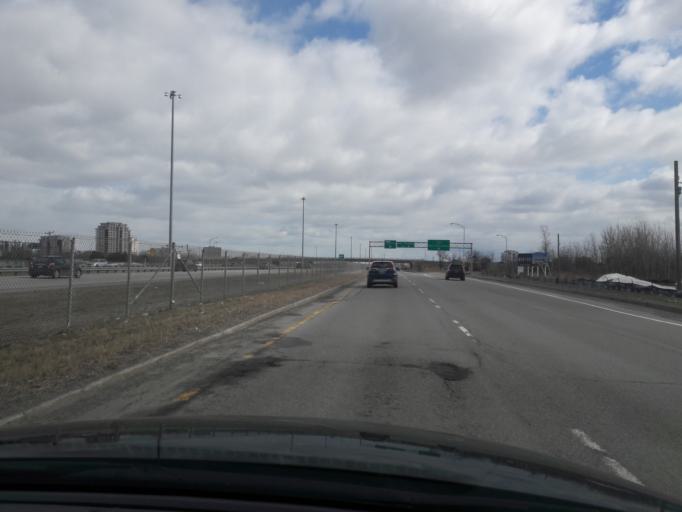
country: CA
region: Quebec
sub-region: Laurentides
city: Rosemere
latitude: 45.5622
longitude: -73.7817
